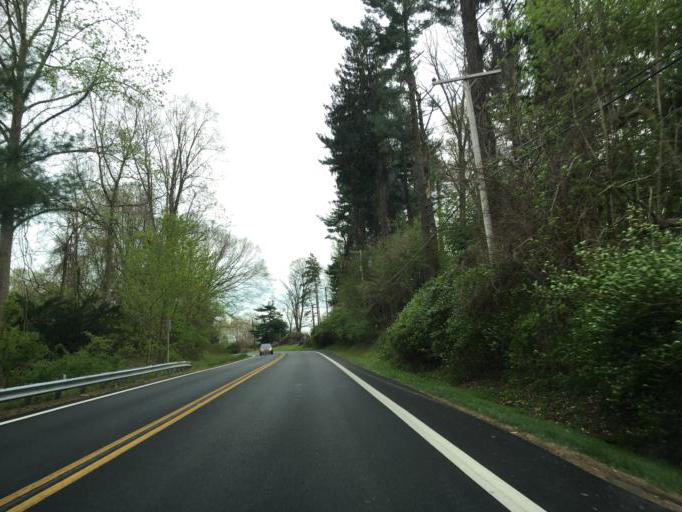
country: US
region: Maryland
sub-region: Baltimore County
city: Hampton
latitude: 39.4700
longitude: -76.5762
